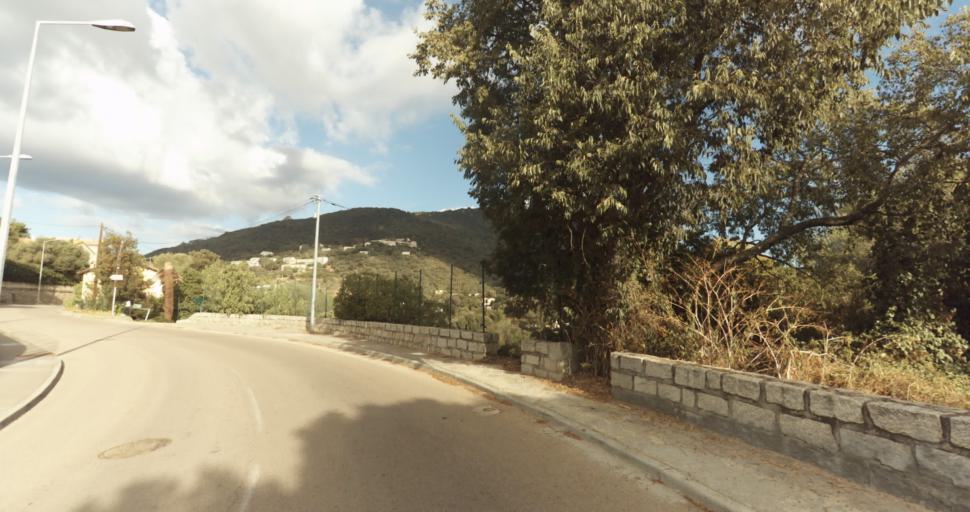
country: FR
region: Corsica
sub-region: Departement de la Corse-du-Sud
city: Ajaccio
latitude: 41.9310
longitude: 8.7263
